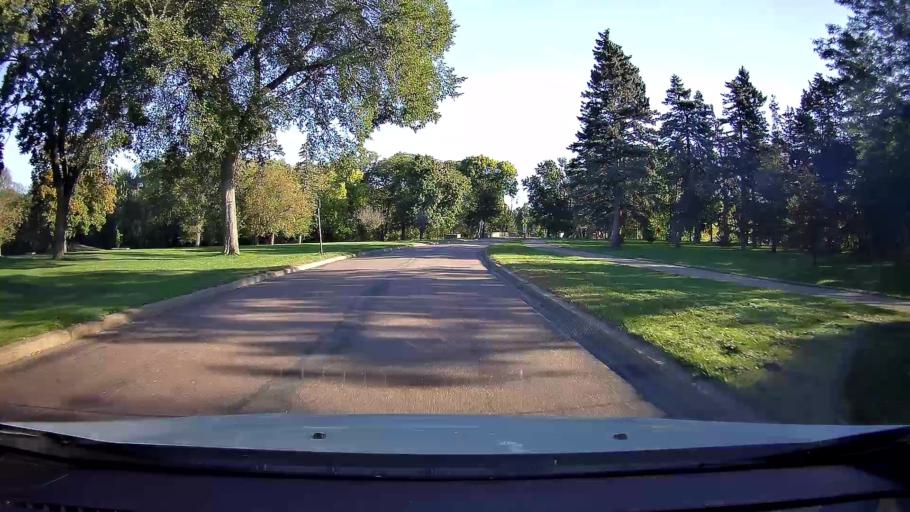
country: US
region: Minnesota
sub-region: Hennepin County
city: Richfield
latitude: 44.9143
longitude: -93.2429
